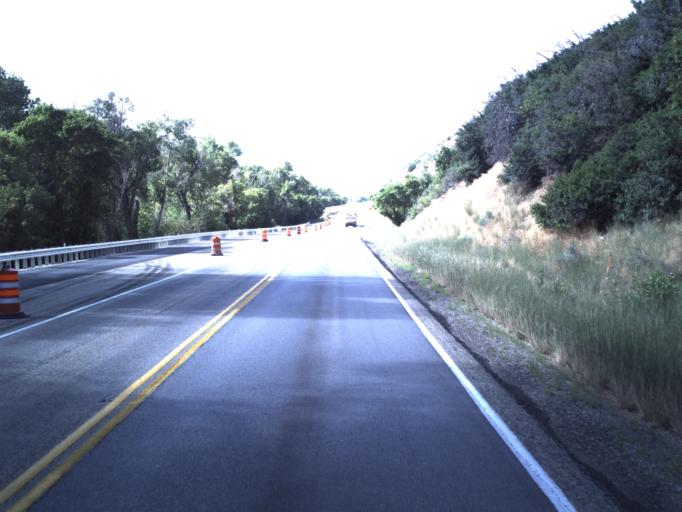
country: US
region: Utah
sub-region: Wasatch County
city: Heber
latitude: 40.4290
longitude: -111.3500
